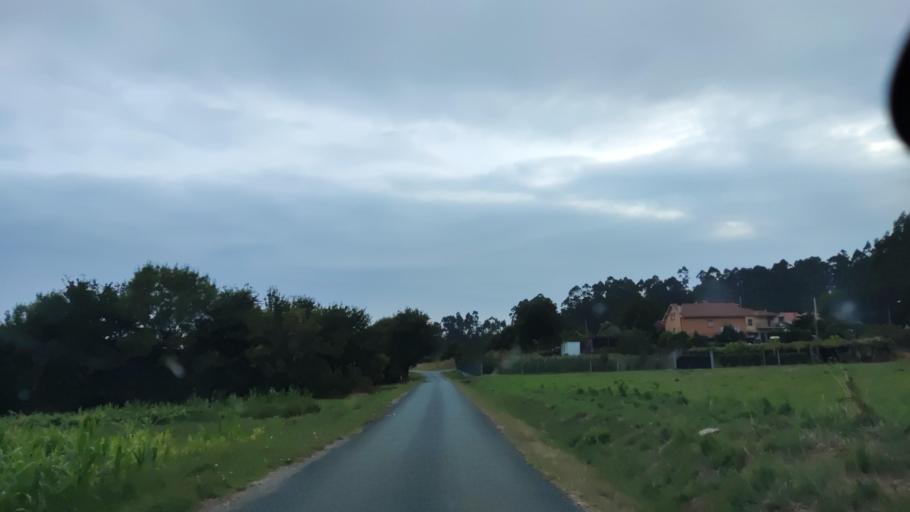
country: ES
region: Galicia
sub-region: Provincia da Coruna
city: Padron
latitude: 42.7247
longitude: -8.6756
